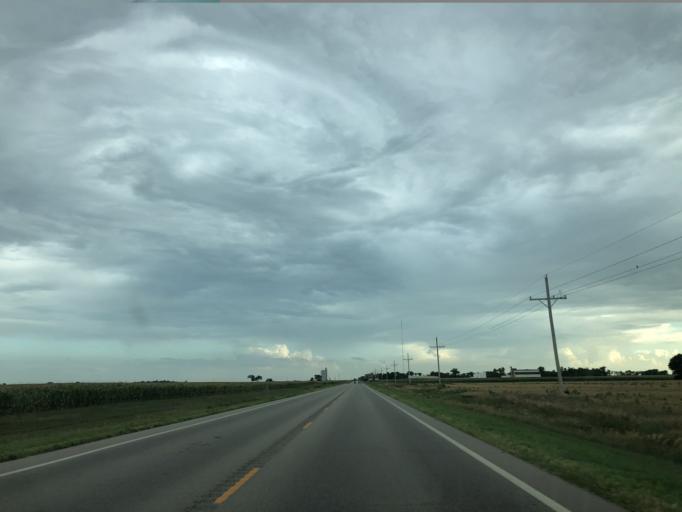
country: US
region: Kansas
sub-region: Rice County
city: Lyons
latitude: 38.2854
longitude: -98.2020
